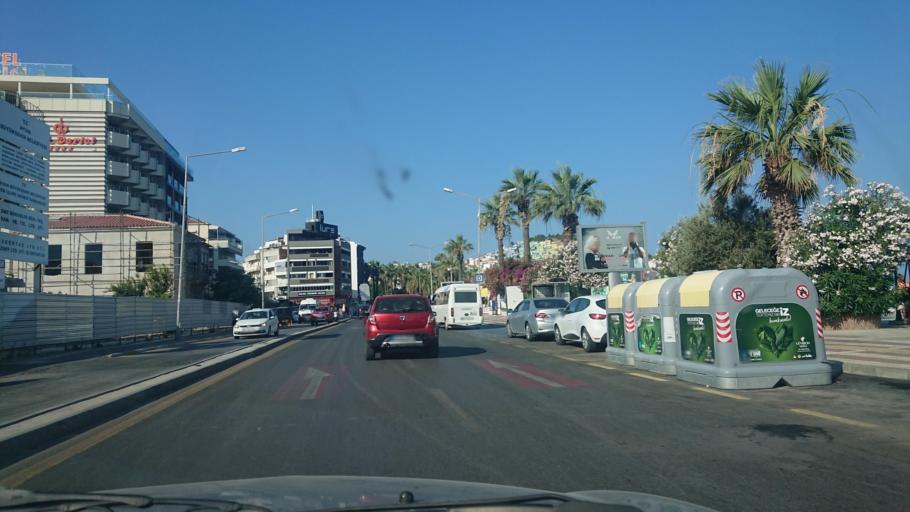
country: TR
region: Aydin
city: Kusadasi
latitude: 37.8637
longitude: 27.2620
